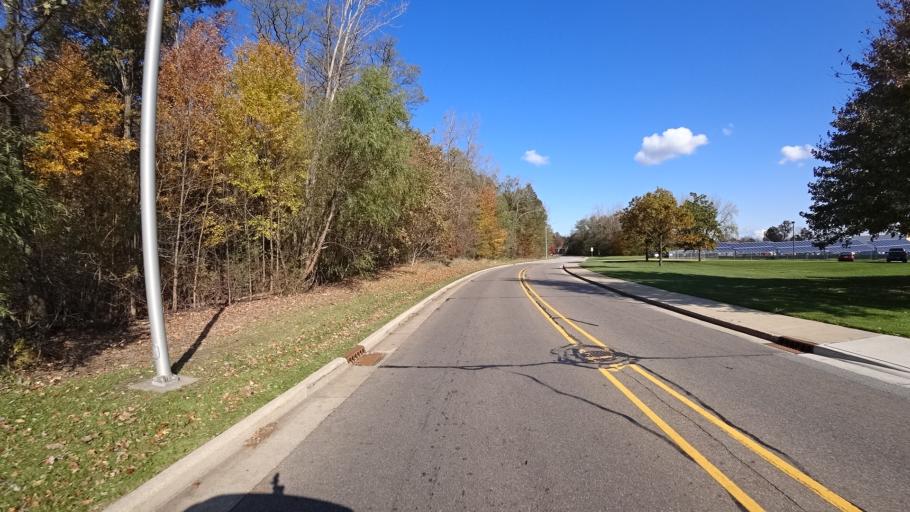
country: US
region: Indiana
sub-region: LaPorte County
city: Michigan City
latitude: 41.6823
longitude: -86.8852
